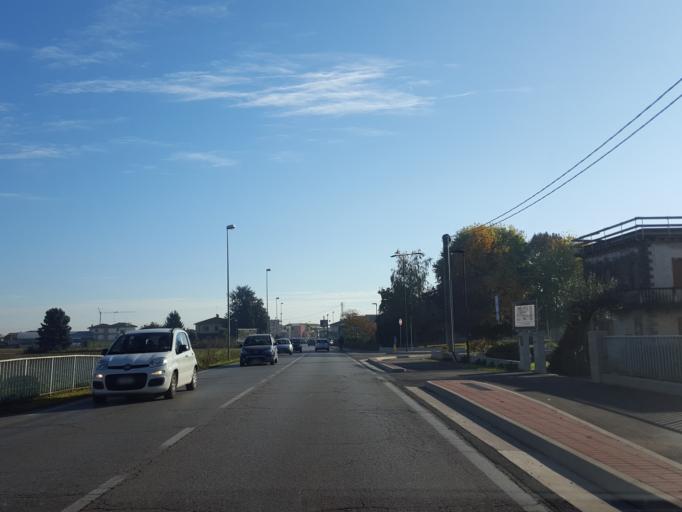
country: IT
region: Veneto
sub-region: Provincia di Vicenza
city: Grumolo delle Abbadesse
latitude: 45.5209
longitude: 11.6859
